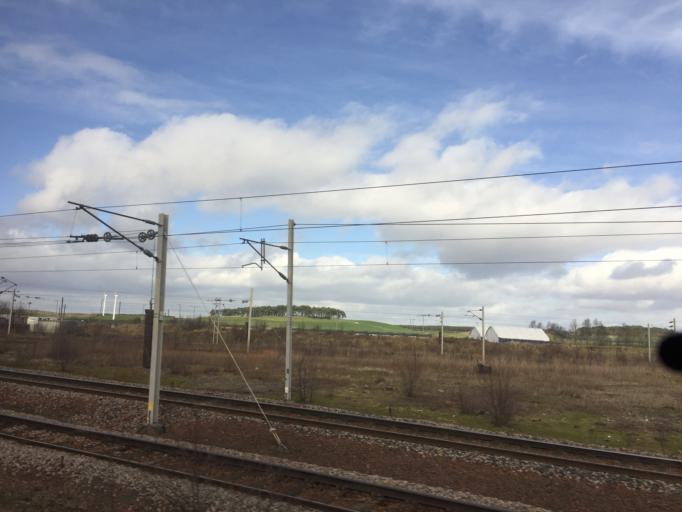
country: GB
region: Scotland
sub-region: South Lanarkshire
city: Carnwath
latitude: 55.6895
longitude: -3.6639
